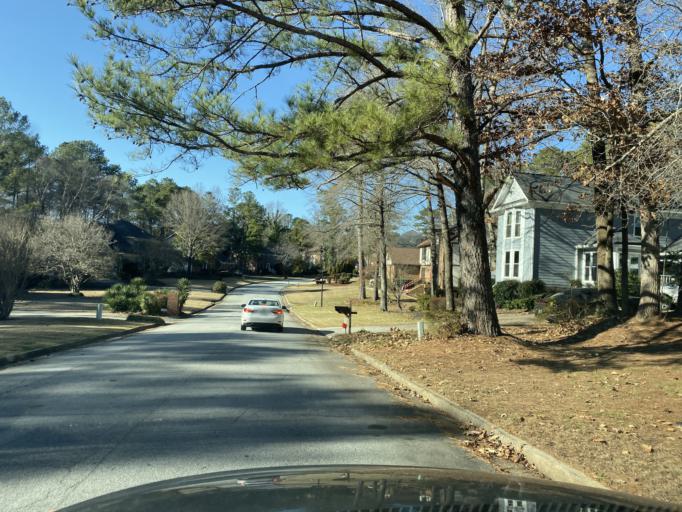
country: US
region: Georgia
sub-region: DeKalb County
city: Pine Mountain
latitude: 33.6801
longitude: -84.1591
